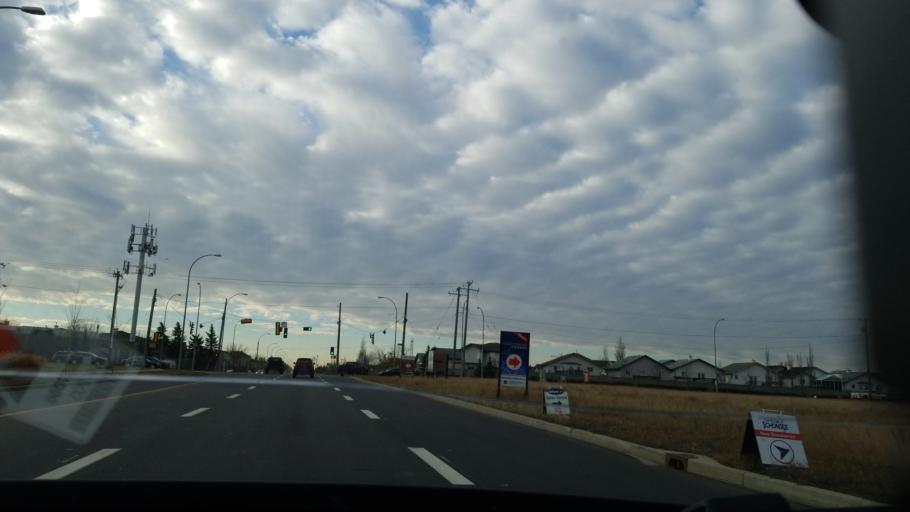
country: CA
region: Alberta
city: Edmonton
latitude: 53.6296
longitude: -113.4429
